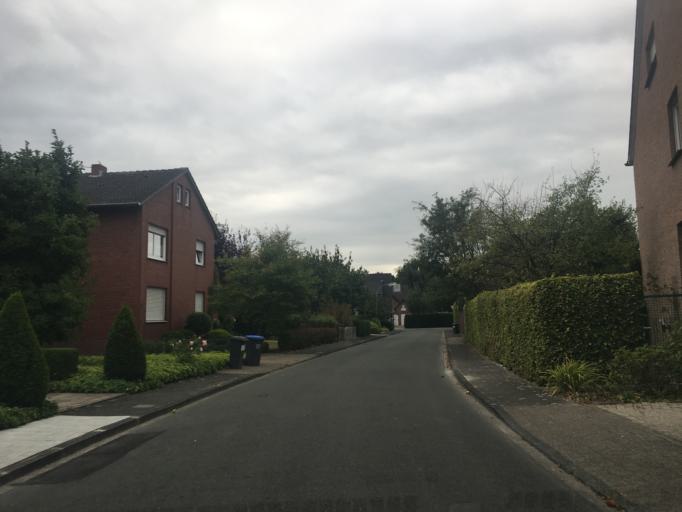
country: DE
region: North Rhine-Westphalia
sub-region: Regierungsbezirk Munster
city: Muenster
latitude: 51.9501
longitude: 7.5337
